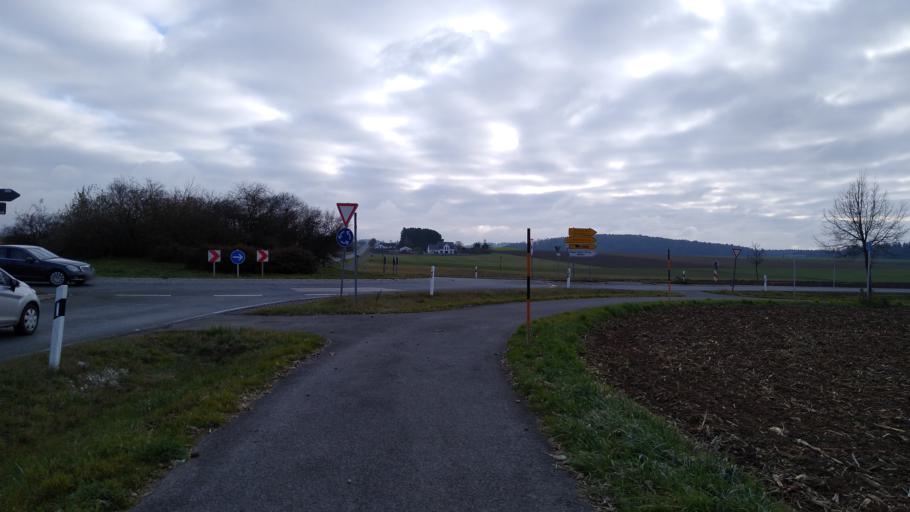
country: DE
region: Bavaria
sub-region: Upper Palatinate
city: Seubersdorf
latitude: 49.1573
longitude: 11.6327
